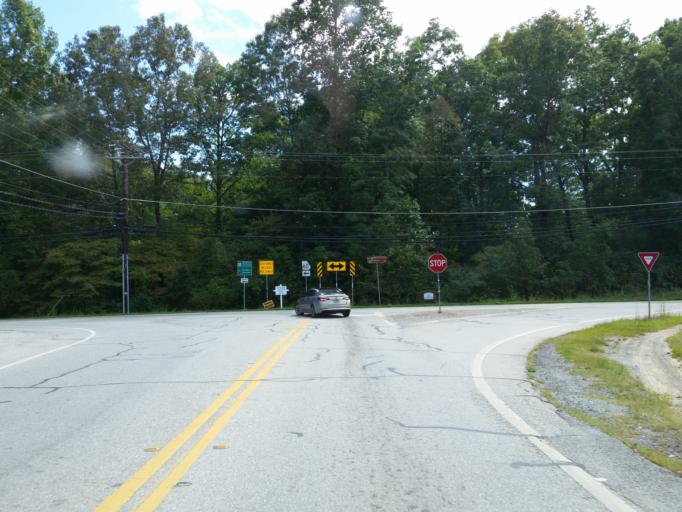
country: US
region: Georgia
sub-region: Fannin County
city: Blue Ridge
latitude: 34.8859
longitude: -84.2620
